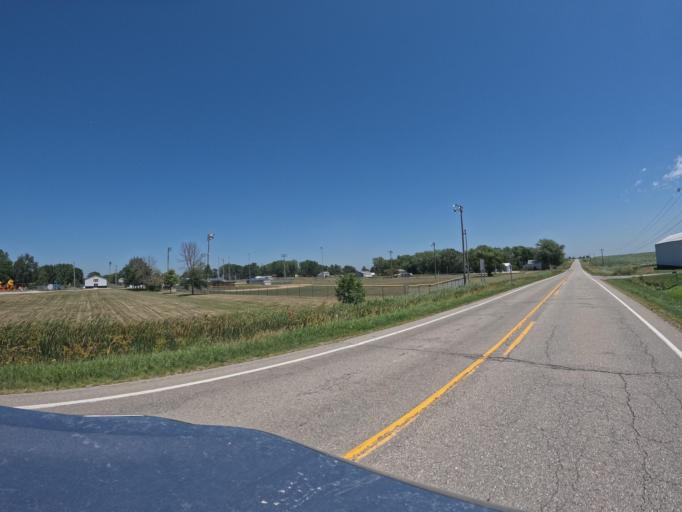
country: US
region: Iowa
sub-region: Keokuk County
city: Sigourney
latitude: 41.4522
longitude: -92.3334
